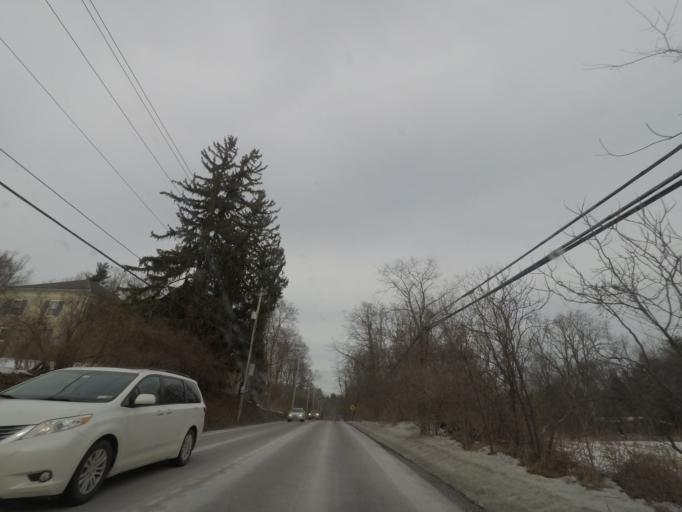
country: US
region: New York
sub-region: Albany County
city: Voorheesville
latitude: 42.5838
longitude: -73.9248
